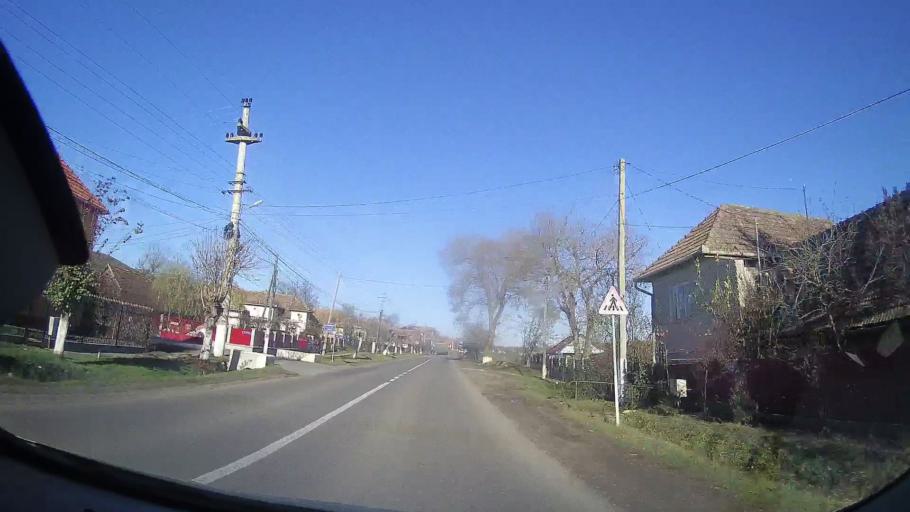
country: RO
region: Mures
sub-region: Comuna Sarmasu
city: Balda
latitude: 46.7239
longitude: 24.1432
